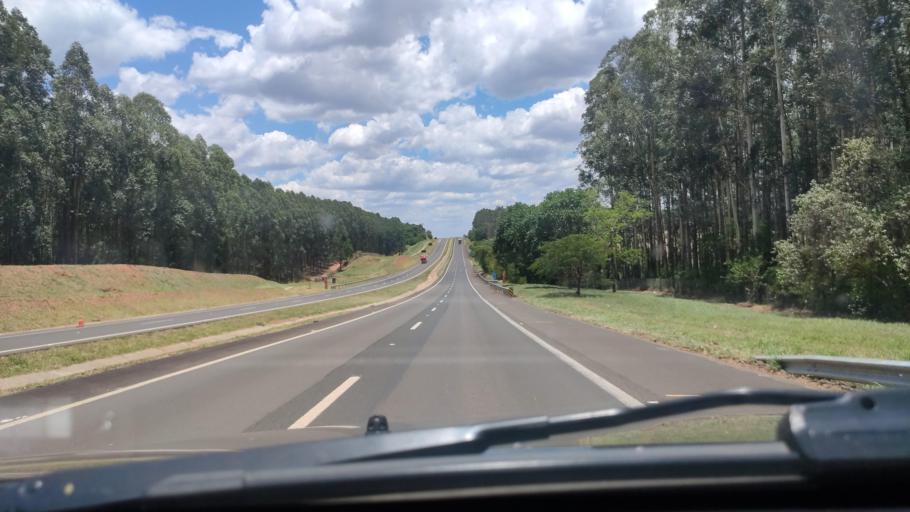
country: BR
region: Sao Paulo
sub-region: Duartina
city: Duartina
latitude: -22.4917
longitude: -49.2530
